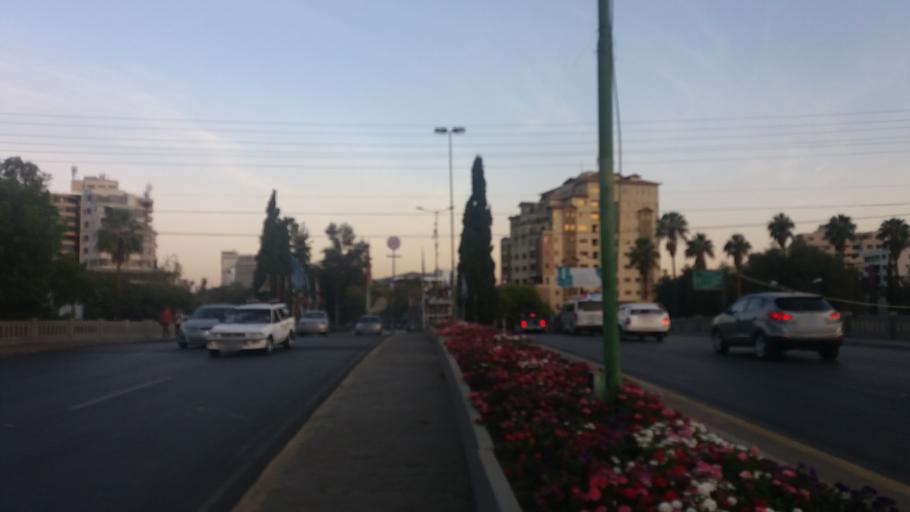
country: BO
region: Cochabamba
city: Cochabamba
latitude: -17.3813
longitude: -66.1602
